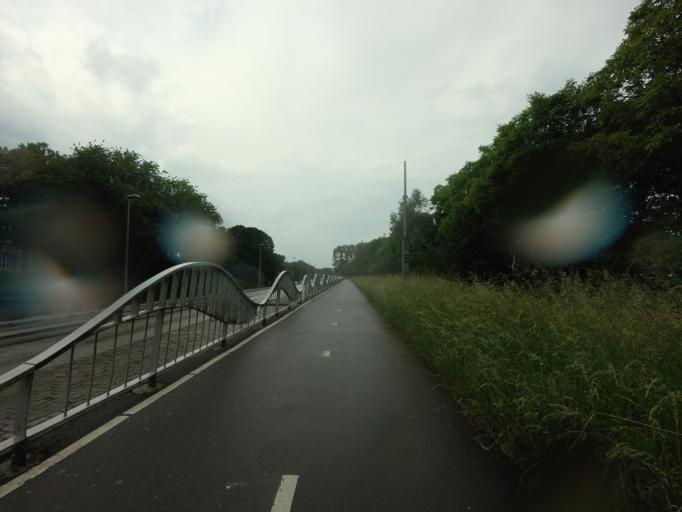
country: NL
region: Utrecht
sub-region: Gemeente Utrecht
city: Utrecht
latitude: 52.1123
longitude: 5.1006
